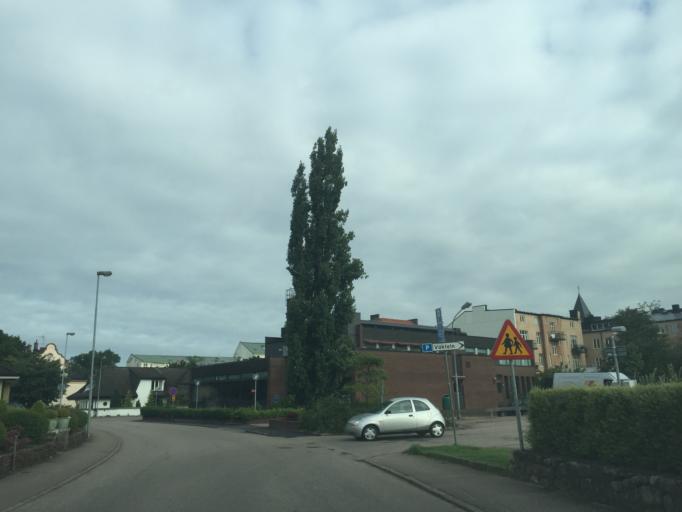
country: SE
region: Skane
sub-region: Angelholms Kommun
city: AEngelholm
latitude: 56.2419
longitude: 12.8605
